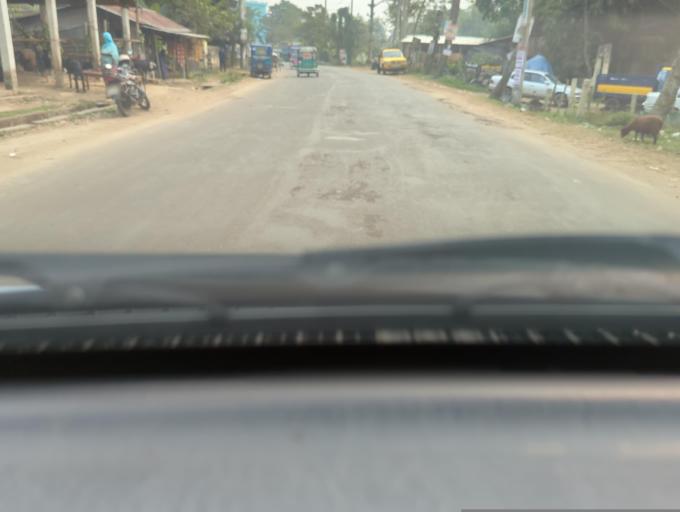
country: BD
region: Sylhet
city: Maulavi Bazar
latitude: 24.4900
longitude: 91.7475
